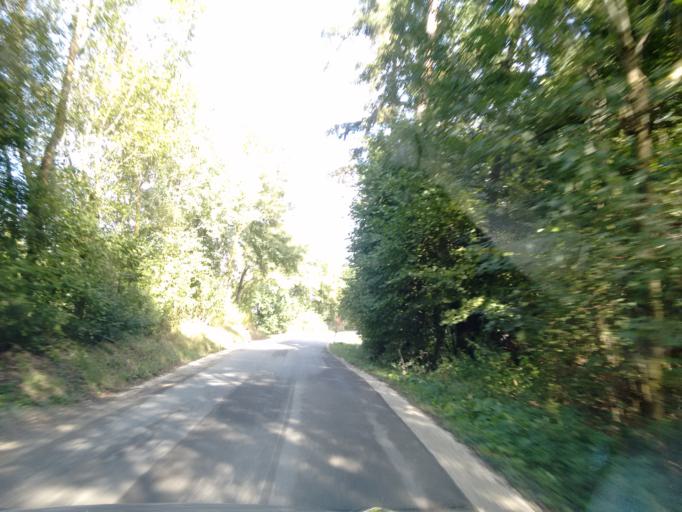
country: AT
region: Upper Austria
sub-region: Politischer Bezirk Kirchdorf an der Krems
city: Kremsmunster
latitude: 48.1081
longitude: 14.1752
